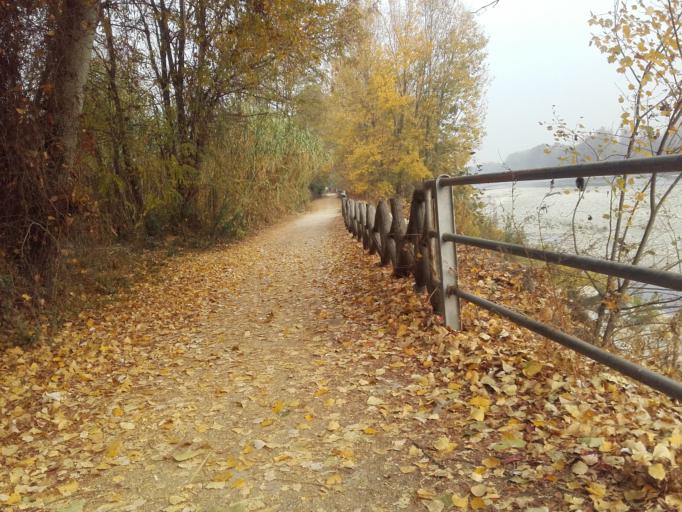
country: IT
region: Piedmont
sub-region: Provincia di Torino
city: San Mauro Torinese
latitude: 45.1049
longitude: 7.7627
